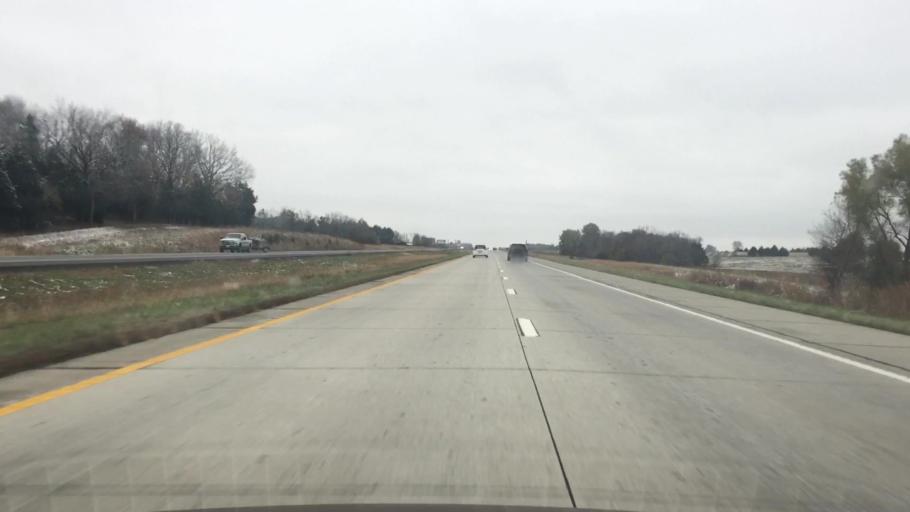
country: US
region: Missouri
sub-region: Saint Clair County
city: Osceola
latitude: 38.0034
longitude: -93.6560
